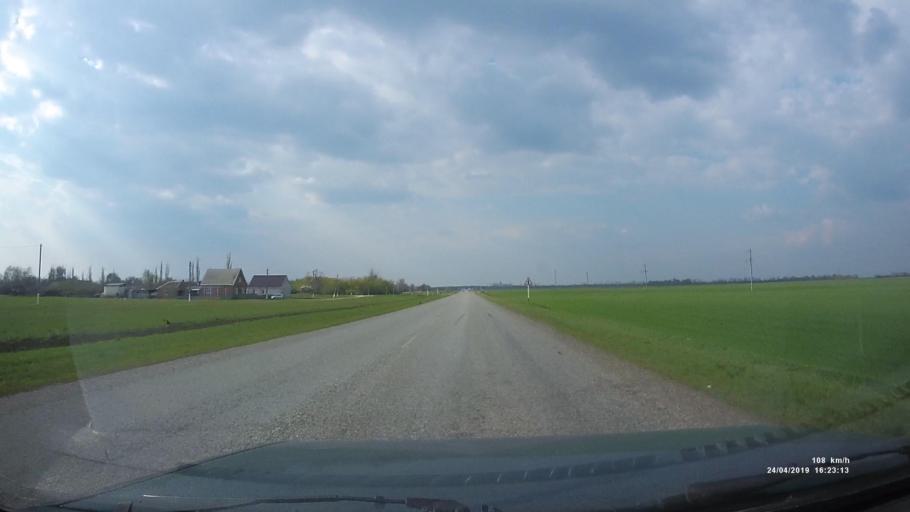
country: RU
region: Rostov
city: Orlovskiy
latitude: 46.8314
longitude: 42.0508
